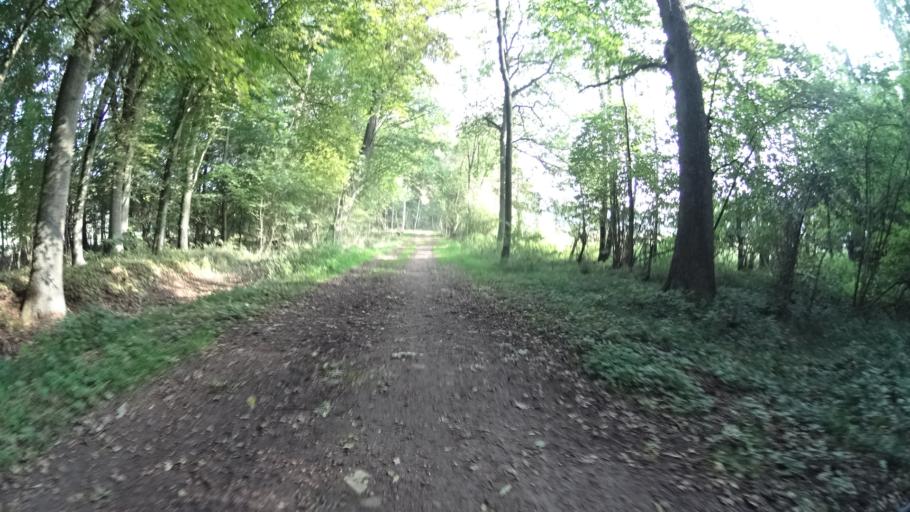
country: DE
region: Lower Saxony
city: Reppenstedt
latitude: 53.2279
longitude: 10.3505
